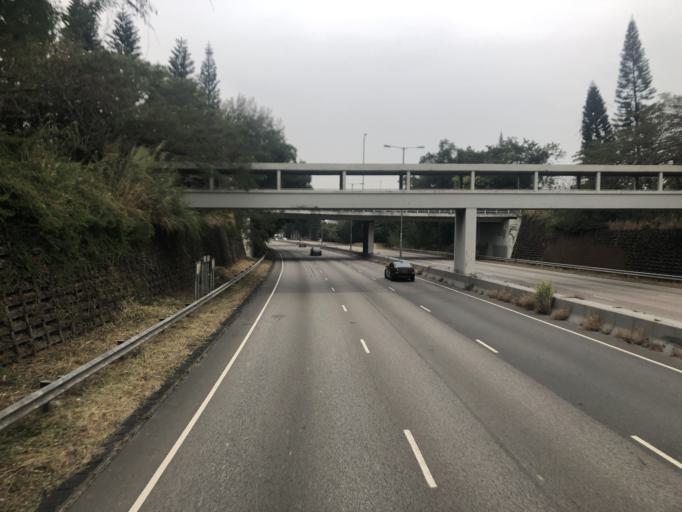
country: CN
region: Guangdong
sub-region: Shenzhen
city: Shenzhen
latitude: 22.5018
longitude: 114.0823
